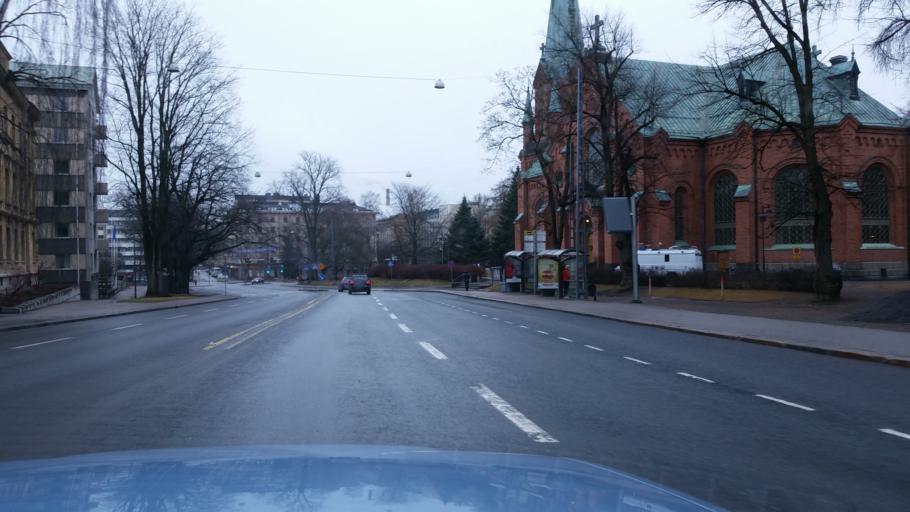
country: FI
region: Pirkanmaa
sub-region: Tampere
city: Tampere
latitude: 61.4976
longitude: 23.7474
